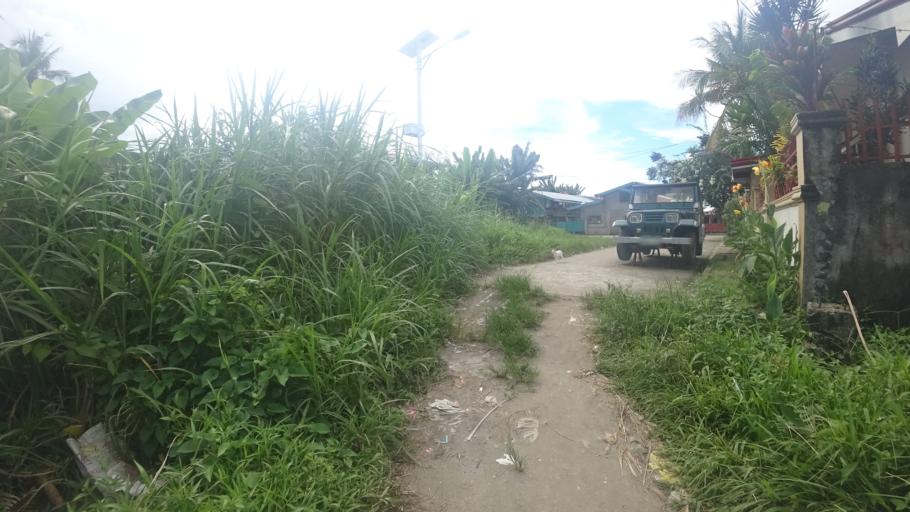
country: PH
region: Eastern Visayas
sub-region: Province of Leyte
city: Baras
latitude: 11.2037
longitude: 125.0095
